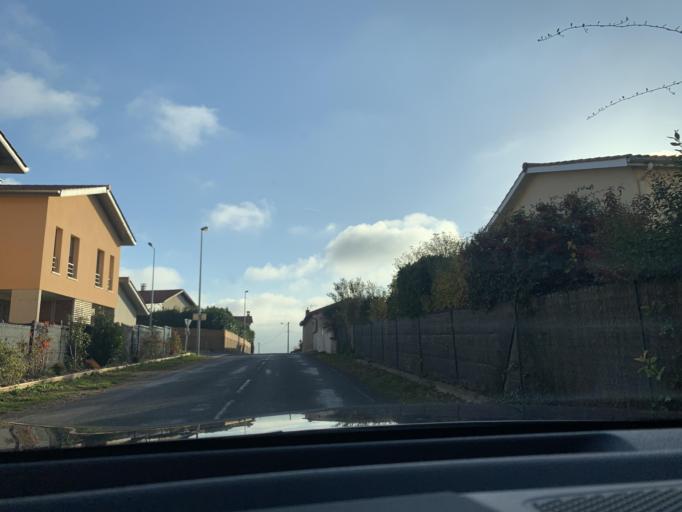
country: FR
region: Rhone-Alpes
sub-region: Departement du Rhone
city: Pommiers
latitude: 45.9509
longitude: 4.6940
